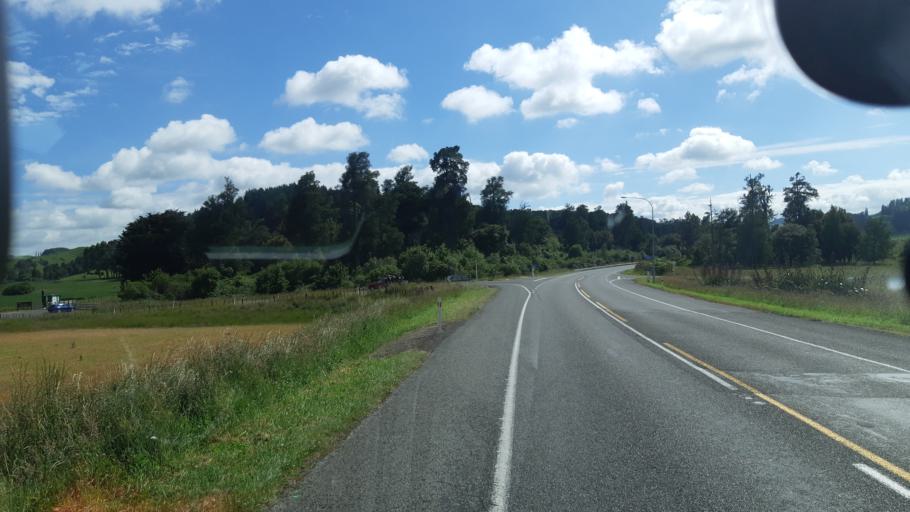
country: NZ
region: Manawatu-Wanganui
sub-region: Rangitikei District
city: Bulls
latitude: -39.9659
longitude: 175.5241
